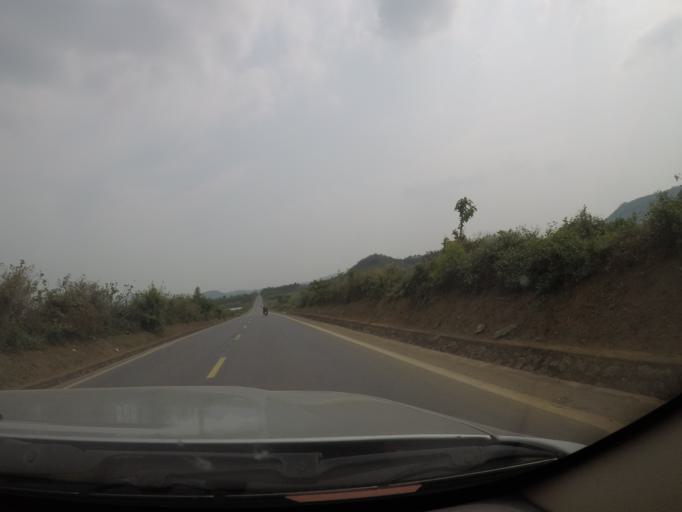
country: VN
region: Thanh Hoa
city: Thi Tran Ben Sung
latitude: 19.3765
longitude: 105.4624
